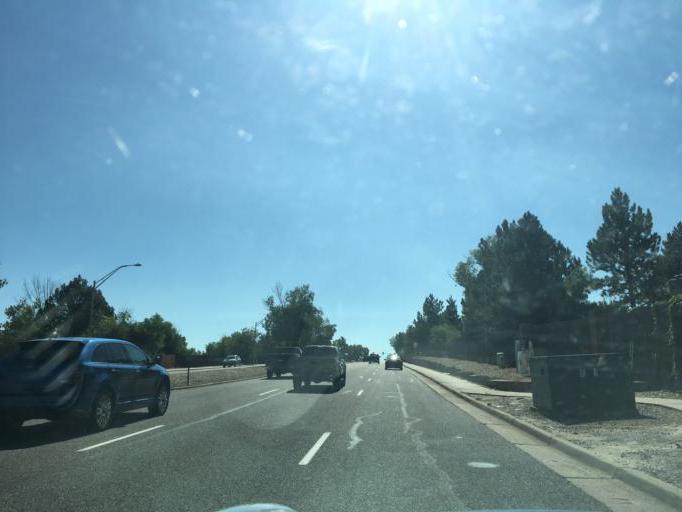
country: US
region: Colorado
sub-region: Arapahoe County
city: Dove Valley
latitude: 39.6304
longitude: -104.8042
